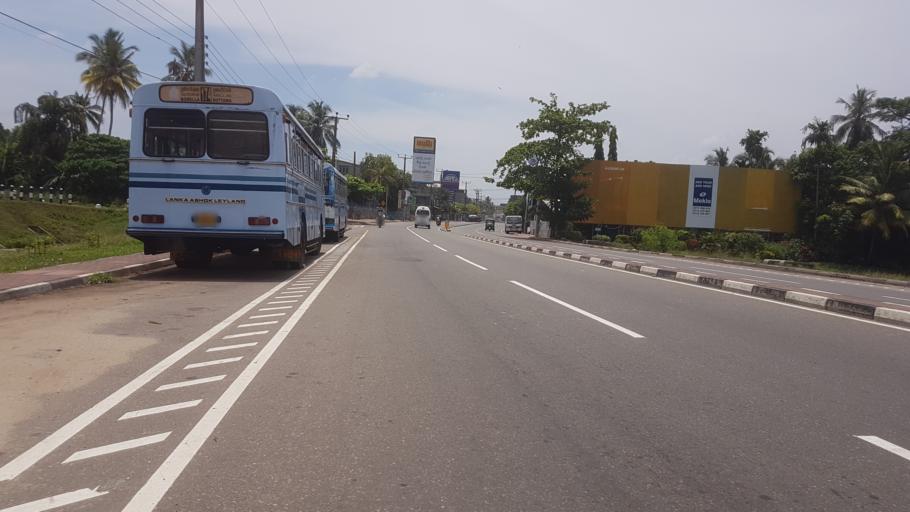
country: LK
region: Western
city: Battaramulla South
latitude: 6.8844
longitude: 79.9326
